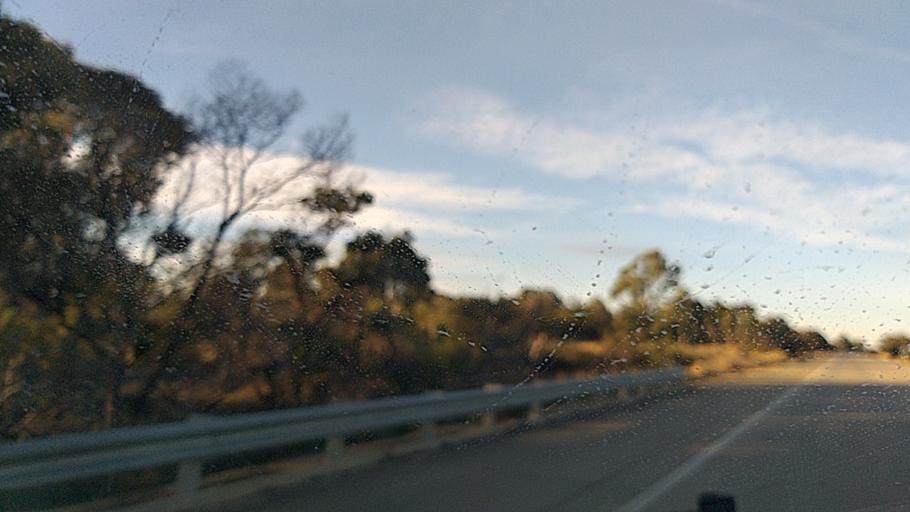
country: AU
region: New South Wales
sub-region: Yass Valley
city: Gundaroo
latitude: -35.1290
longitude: 149.3421
